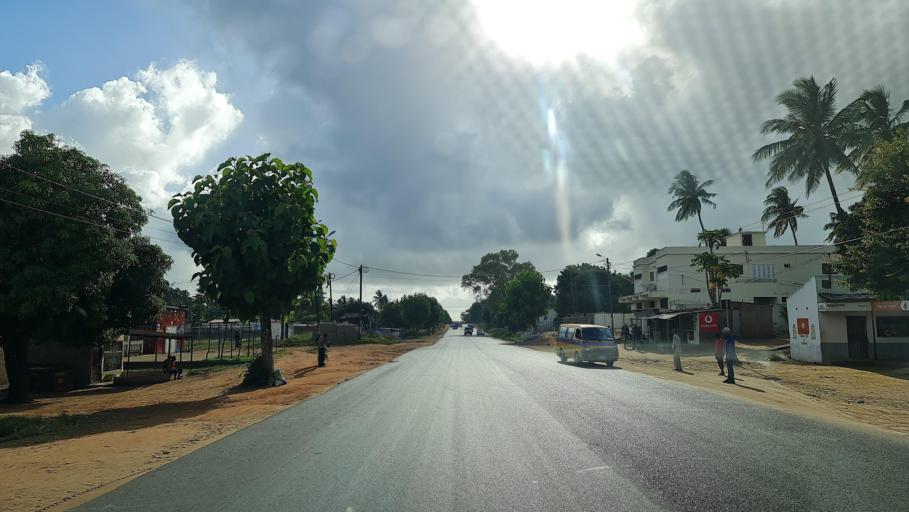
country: MZ
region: Gaza
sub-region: Xai-Xai District
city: Xai-Xai
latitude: -25.0564
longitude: 33.6860
